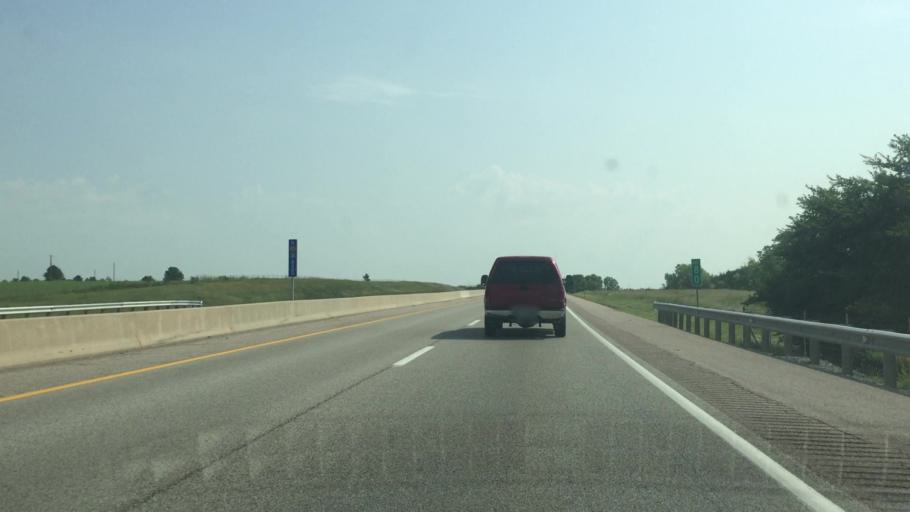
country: US
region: Kansas
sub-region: Butler County
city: El Dorado
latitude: 37.9196
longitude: -96.7943
